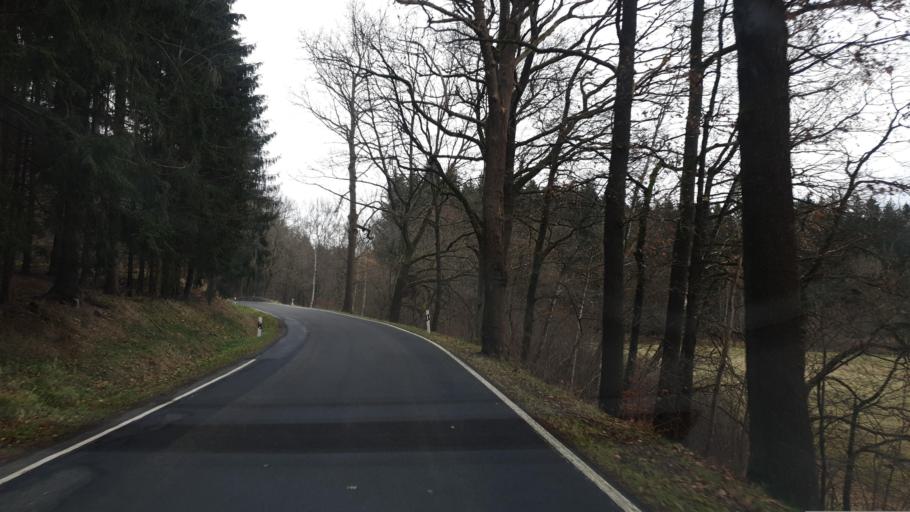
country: DE
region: Saxony
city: Mulda
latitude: 50.7846
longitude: 13.4162
